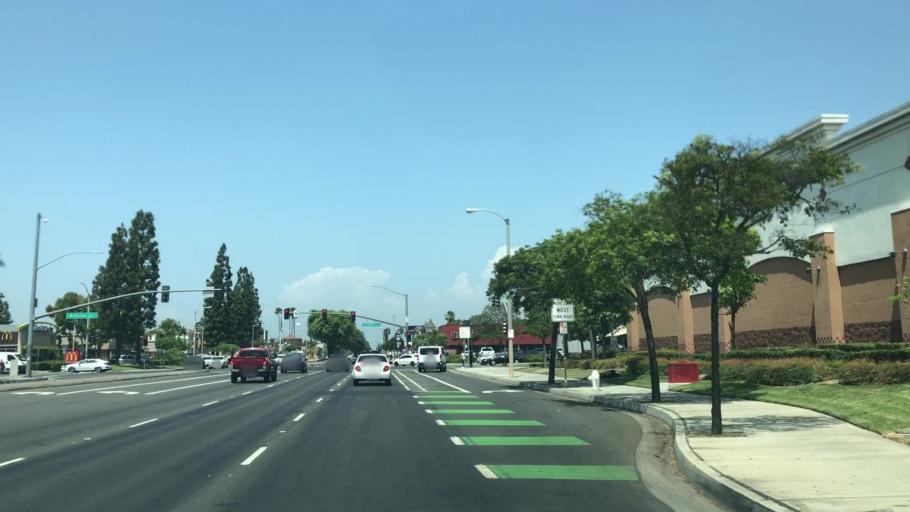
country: US
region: California
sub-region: Orange County
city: Garden Grove
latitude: 33.7374
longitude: -117.9199
